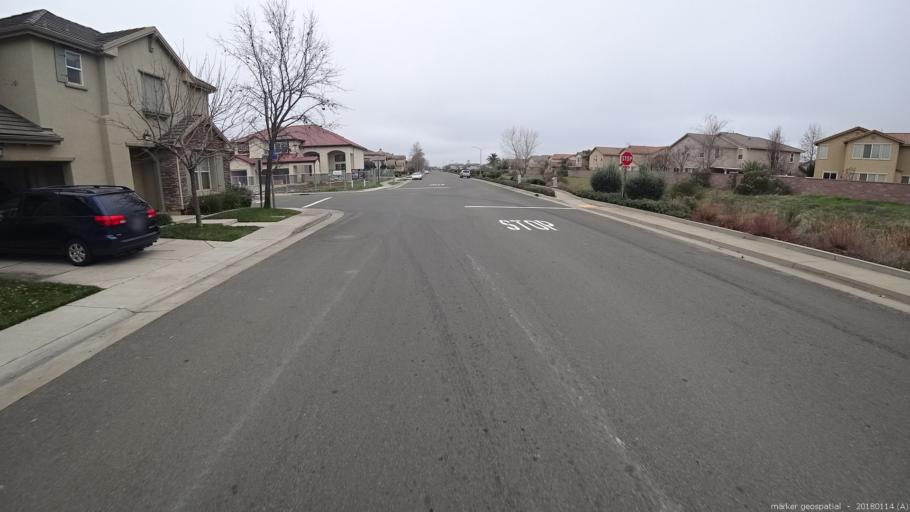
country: US
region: California
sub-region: Sacramento County
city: Rancho Cordova
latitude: 38.5449
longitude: -121.2386
